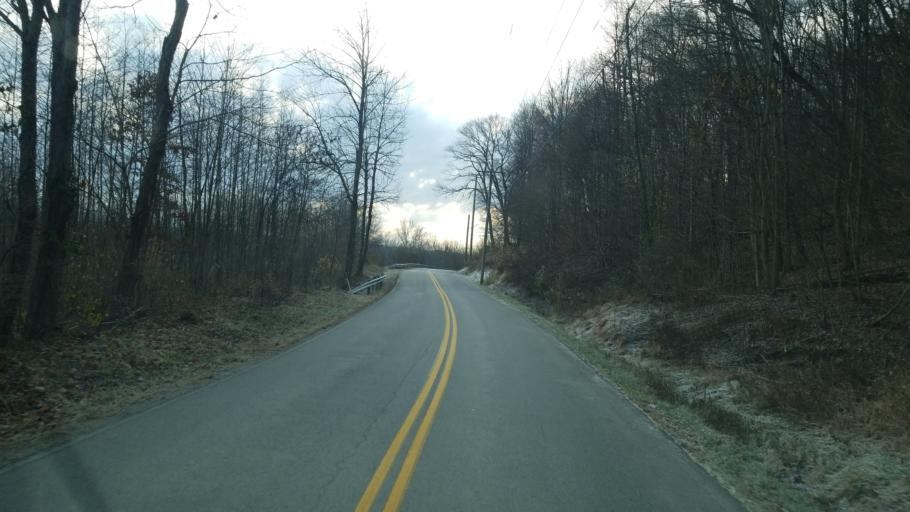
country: US
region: Ohio
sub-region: Pike County
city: Waverly
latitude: 39.2140
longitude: -82.8690
